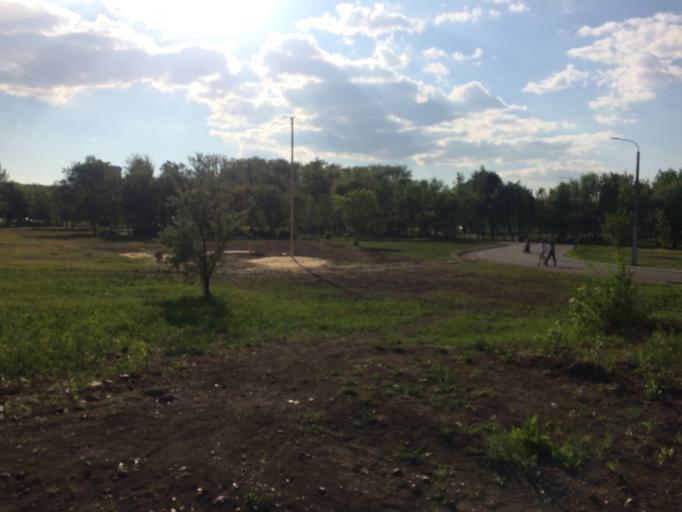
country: RU
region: Chelyabinsk
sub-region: Gorod Magnitogorsk
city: Magnitogorsk
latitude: 53.4012
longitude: 58.9946
